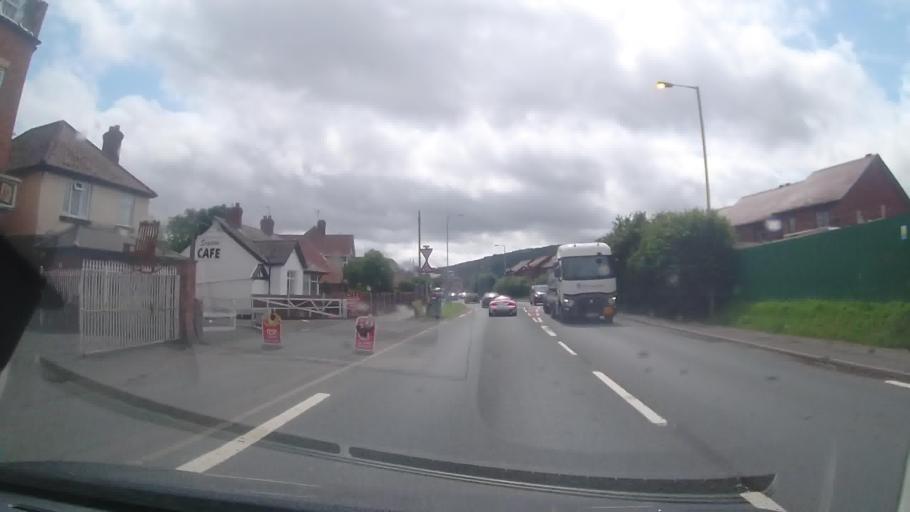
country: GB
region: England
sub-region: Shropshire
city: Craven Arms
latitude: 52.4427
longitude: -2.8357
